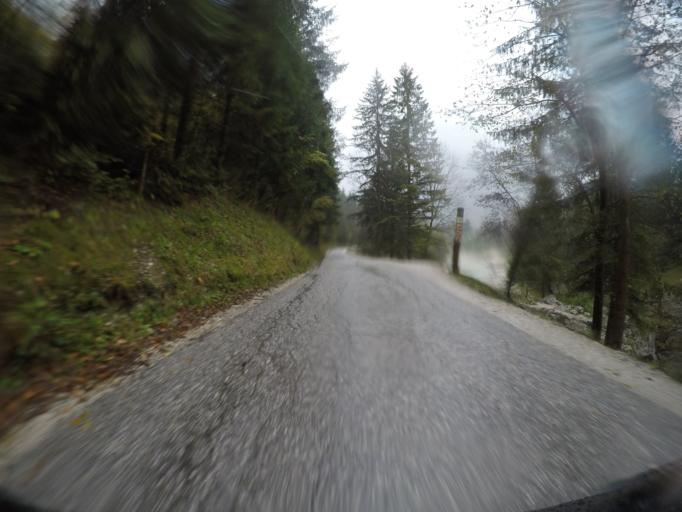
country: SI
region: Bovec
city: Bovec
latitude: 46.3369
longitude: 13.6463
